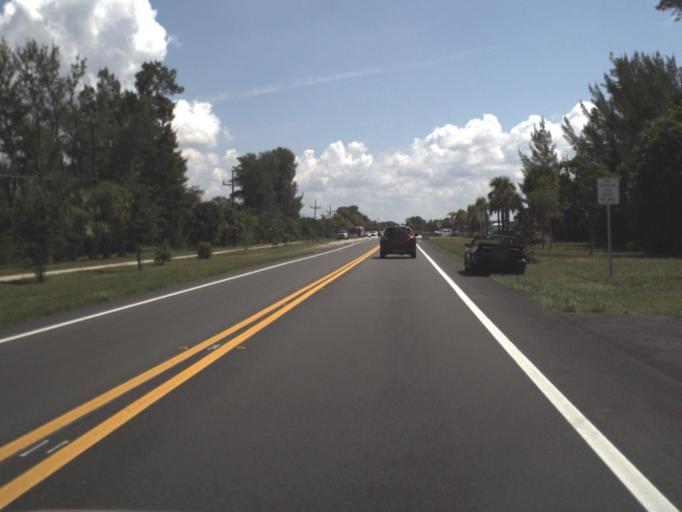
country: US
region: Florida
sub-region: Manatee County
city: Cortez
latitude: 27.4963
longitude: -82.6624
